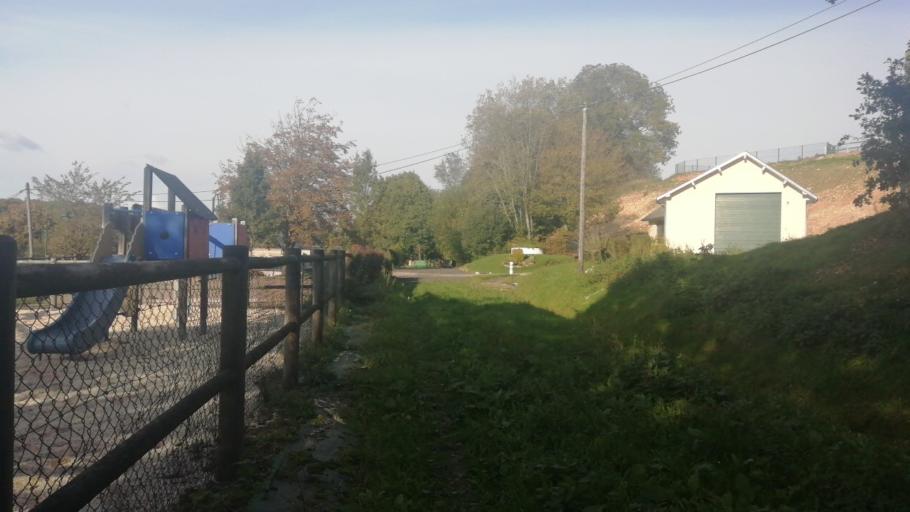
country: FR
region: Haute-Normandie
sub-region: Departement de la Seine-Maritime
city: Rolleville
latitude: 49.5920
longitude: 0.2128
